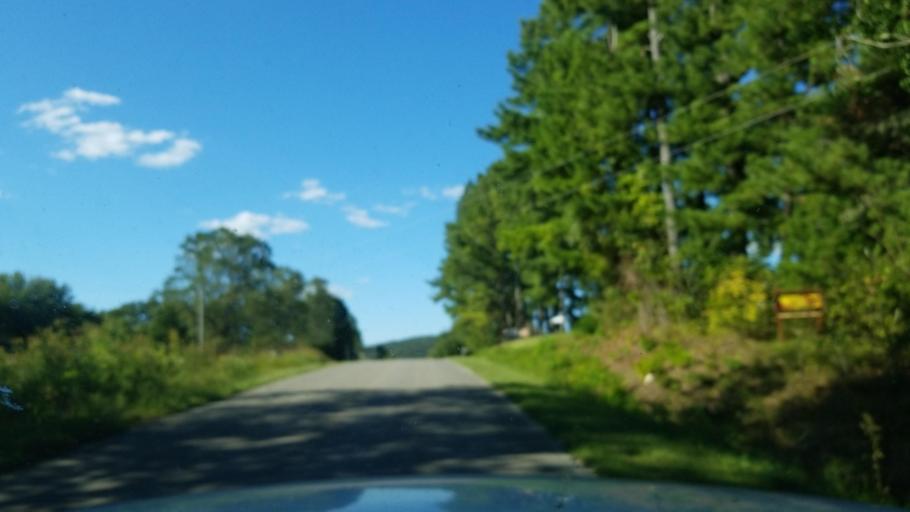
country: US
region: Illinois
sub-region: Hardin County
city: Elizabethtown
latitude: 37.5832
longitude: -88.3655
